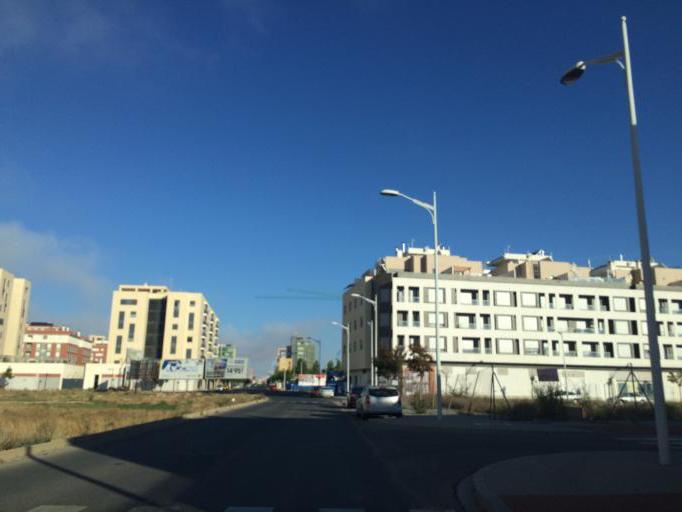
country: ES
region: Castille-La Mancha
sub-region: Provincia de Albacete
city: Albacete
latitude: 39.0040
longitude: -1.8713
